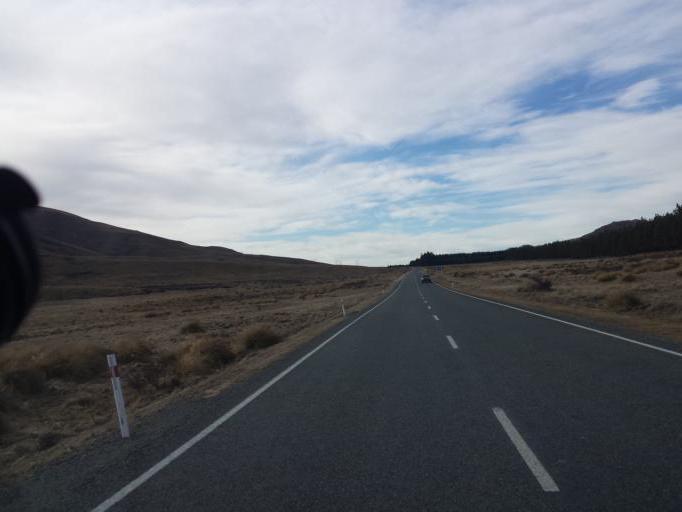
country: NZ
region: Canterbury
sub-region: Timaru District
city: Pleasant Point
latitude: -44.0930
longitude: 170.5737
